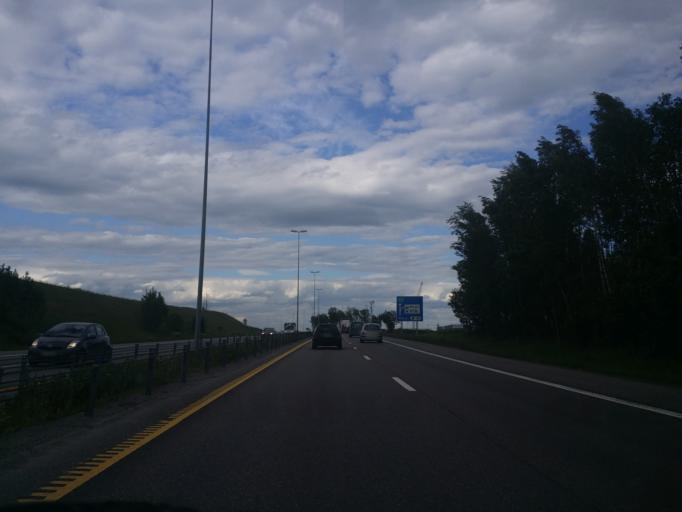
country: NO
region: Akershus
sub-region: Skedsmo
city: Leirsund
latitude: 60.0089
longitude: 11.0545
